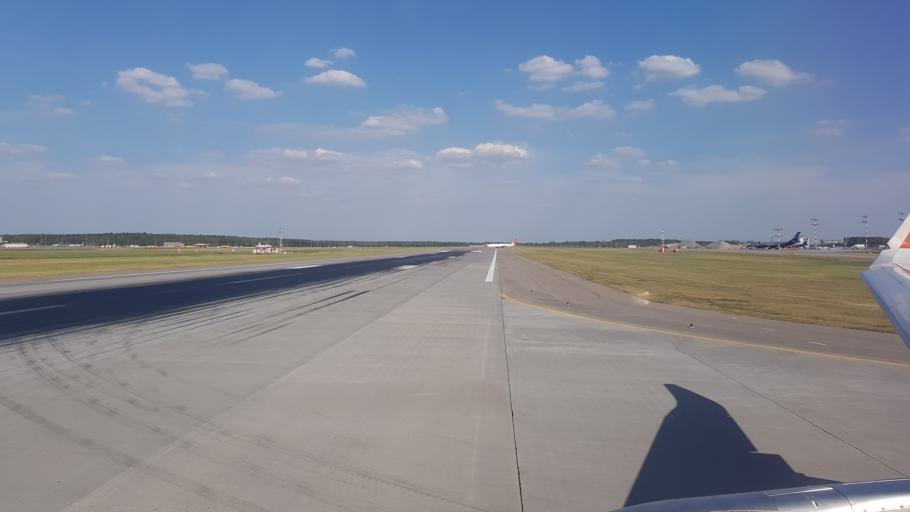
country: RU
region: Moskovskaya
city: Lobnya
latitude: 55.9733
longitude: 37.4301
